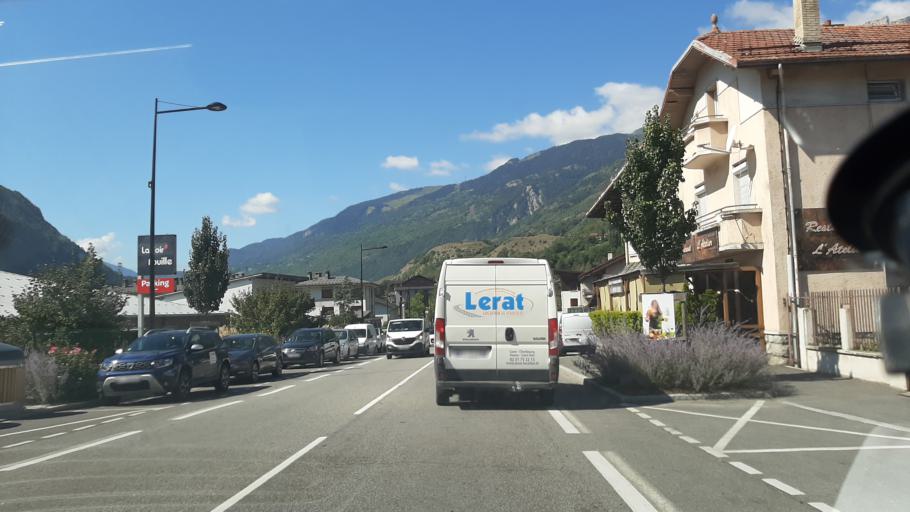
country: FR
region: Rhone-Alpes
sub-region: Departement de la Savoie
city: Aime
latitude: 45.5554
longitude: 6.6464
